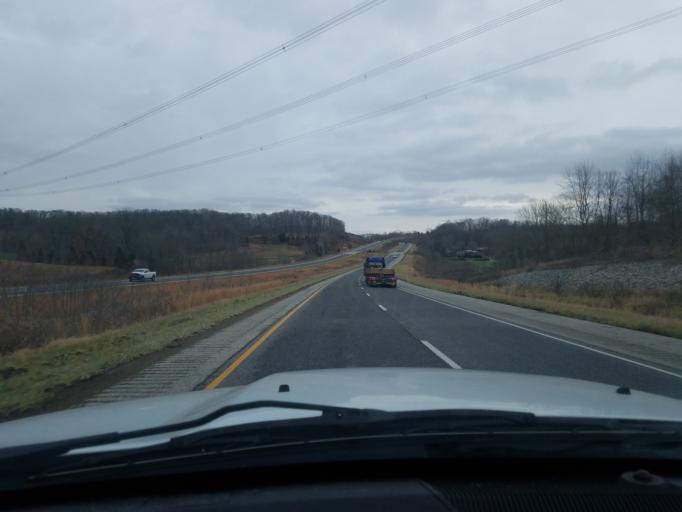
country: US
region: Indiana
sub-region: Dubois County
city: Ferdinand
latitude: 38.2158
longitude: -86.7393
